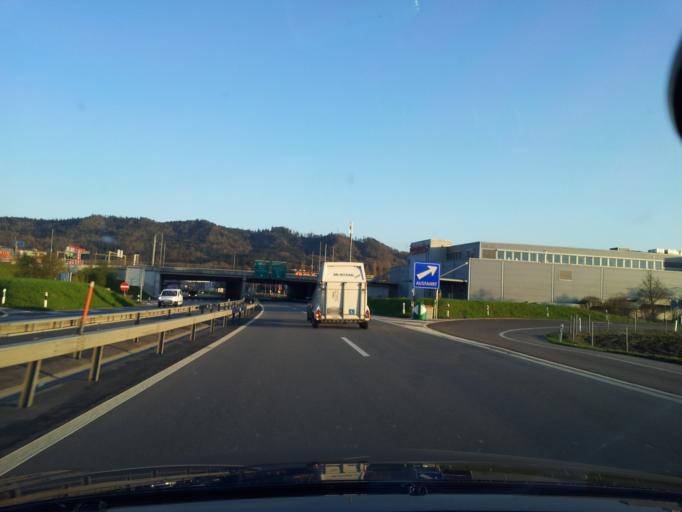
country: CH
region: Bern
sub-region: Bern-Mittelland District
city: Urtenen
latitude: 47.0193
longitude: 7.4887
